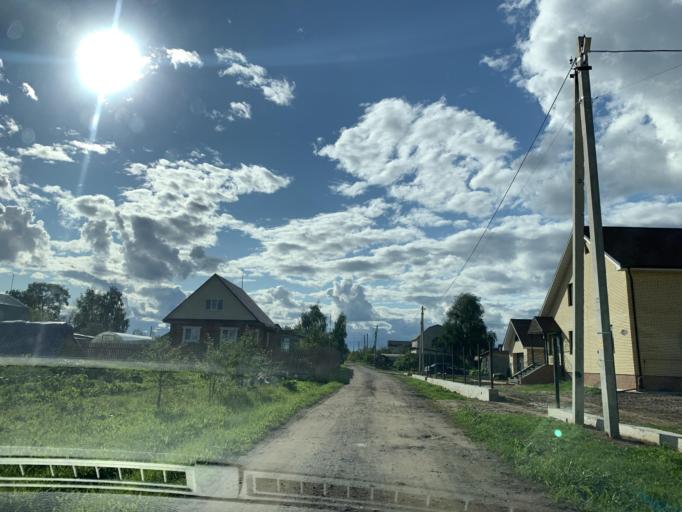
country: RU
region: Jaroslavl
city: Tunoshna
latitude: 57.6627
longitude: 40.0740
